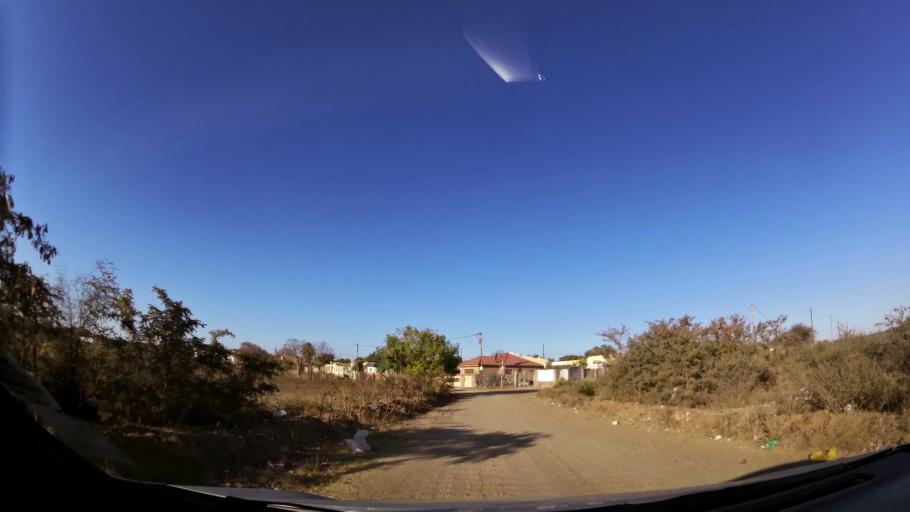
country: ZA
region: Limpopo
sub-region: Capricorn District Municipality
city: Polokwane
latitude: -23.8419
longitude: 29.3590
